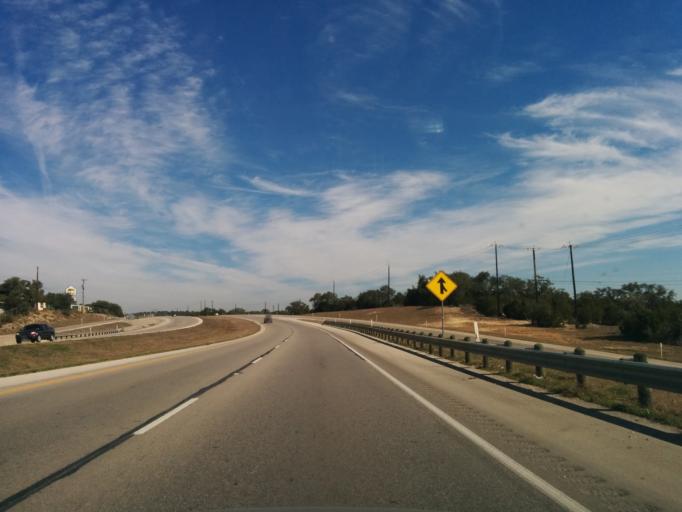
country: US
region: Texas
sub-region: Comal County
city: Bulverde
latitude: 29.7442
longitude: -98.4340
